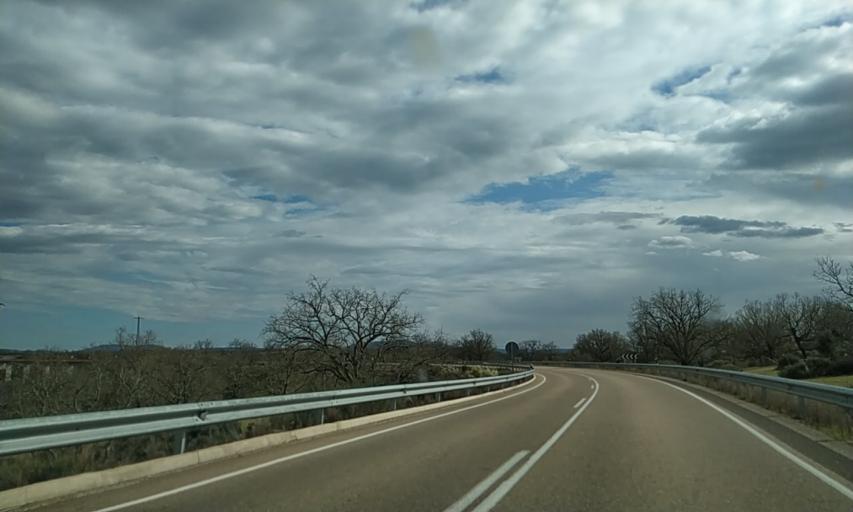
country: ES
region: Castille and Leon
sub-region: Provincia de Salamanca
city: Robleda
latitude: 40.4336
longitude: -6.6051
